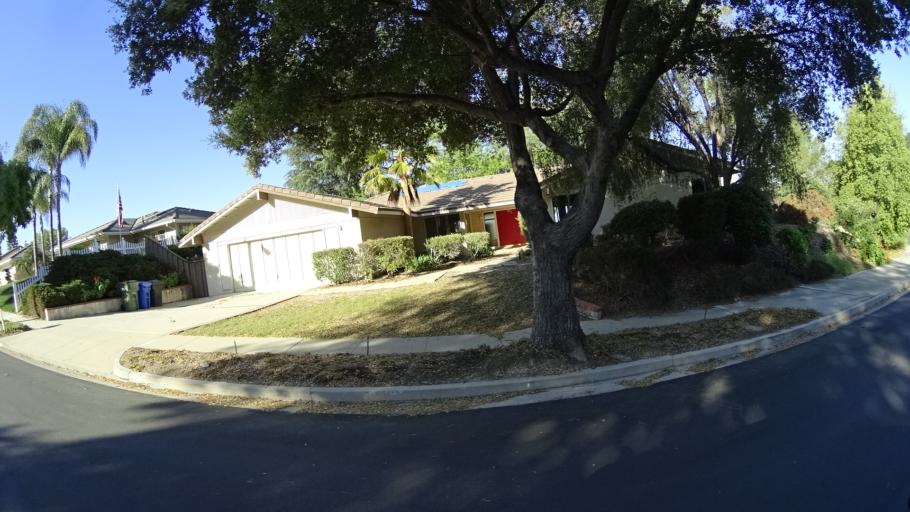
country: US
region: California
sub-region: Ventura County
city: Thousand Oaks
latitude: 34.1951
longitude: -118.8397
